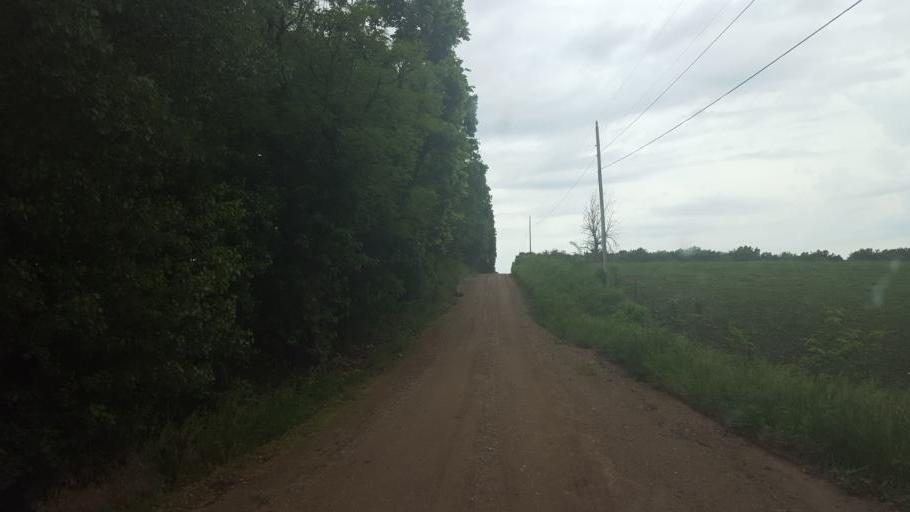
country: US
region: Missouri
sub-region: Moniteau County
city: California
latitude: 38.6763
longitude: -92.5985
